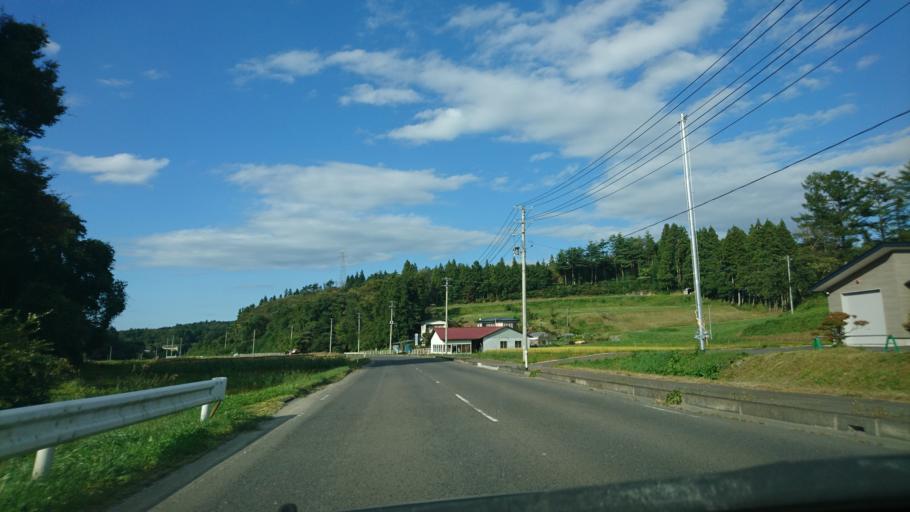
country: JP
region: Iwate
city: Ichinoseki
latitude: 38.8857
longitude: 141.3323
